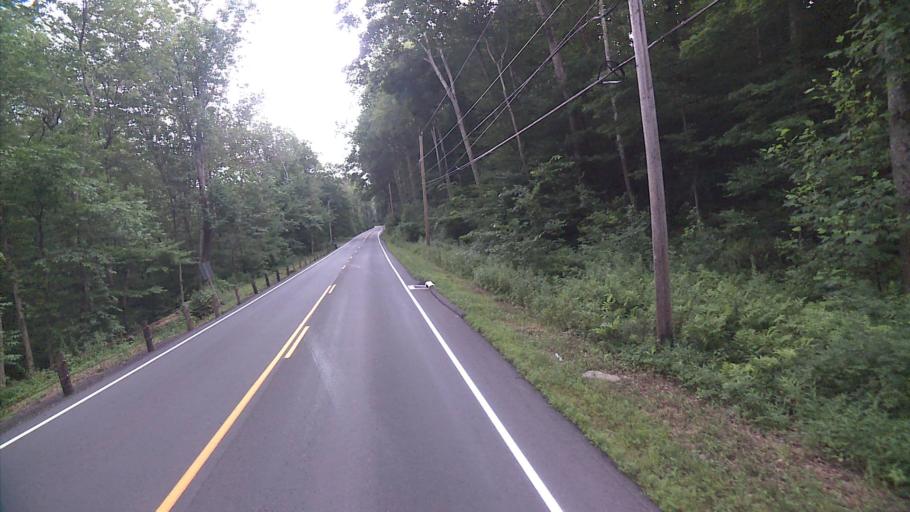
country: US
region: Connecticut
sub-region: New Haven County
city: Heritage Village
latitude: 41.5266
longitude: -73.2705
